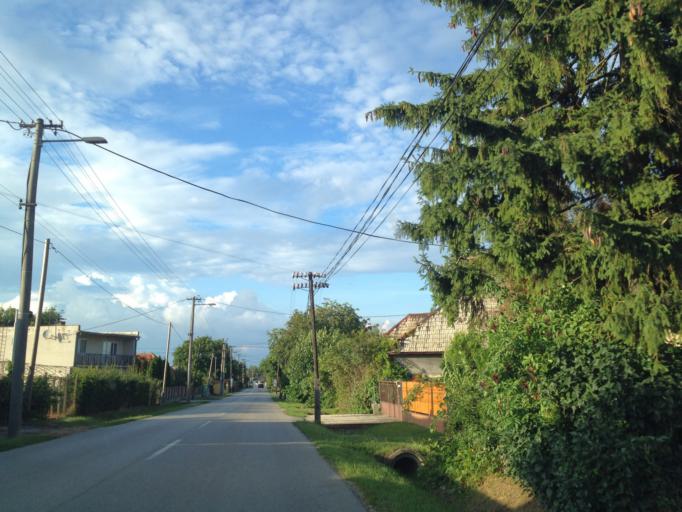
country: SK
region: Nitriansky
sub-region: Okres Komarno
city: Hurbanovo
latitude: 47.8979
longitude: 18.3048
